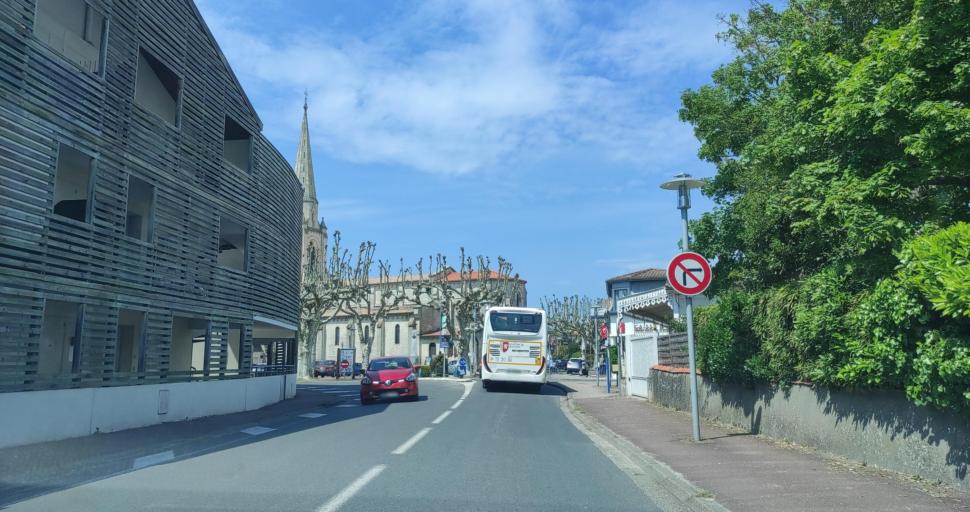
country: FR
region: Aquitaine
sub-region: Departement de la Gironde
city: Ares
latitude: 44.7667
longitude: -1.1391
